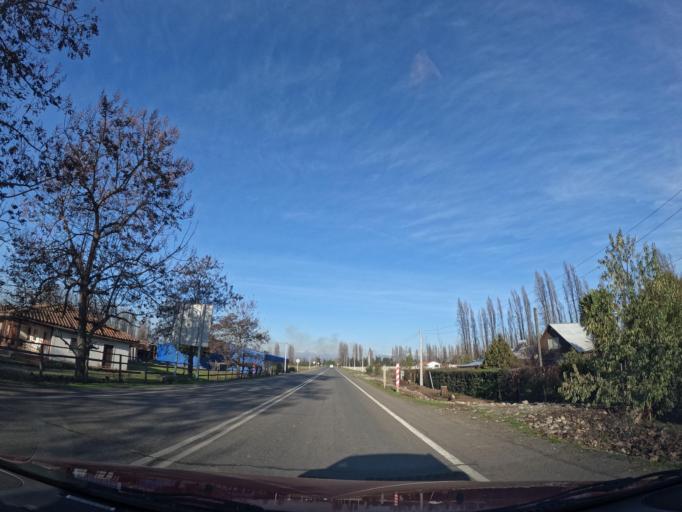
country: CL
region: Maule
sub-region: Provincia de Talca
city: San Clemente
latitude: -35.6244
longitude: -71.4816
